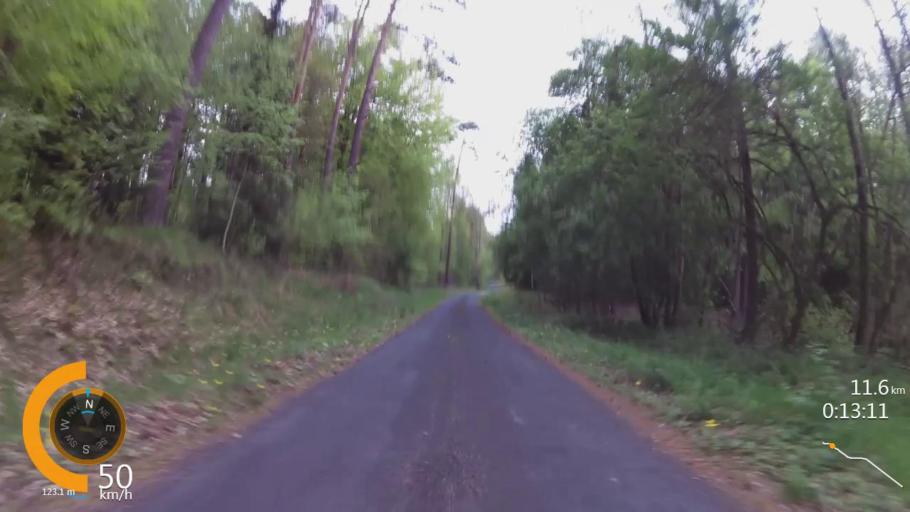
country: PL
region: West Pomeranian Voivodeship
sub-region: Powiat drawski
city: Wierzchowo
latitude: 53.5249
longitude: 16.0975
